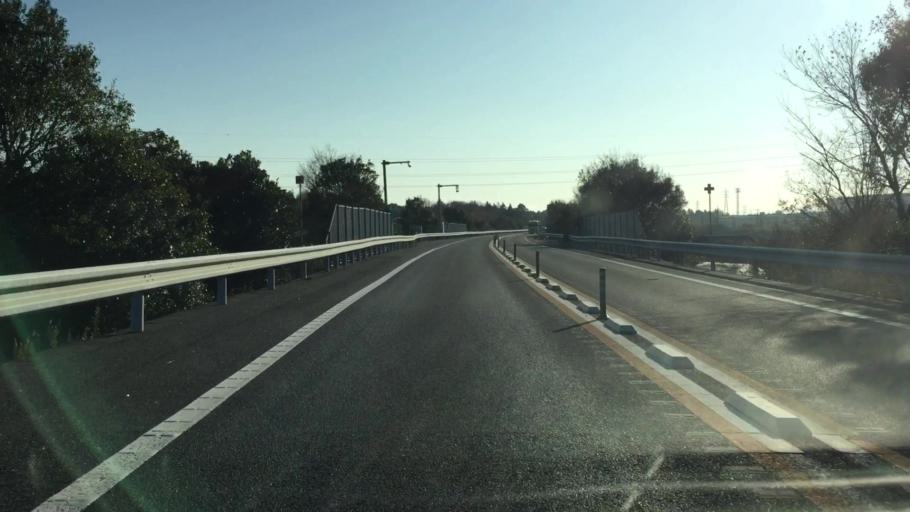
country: JP
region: Ibaraki
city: Ami
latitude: 35.9945
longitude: 140.2121
